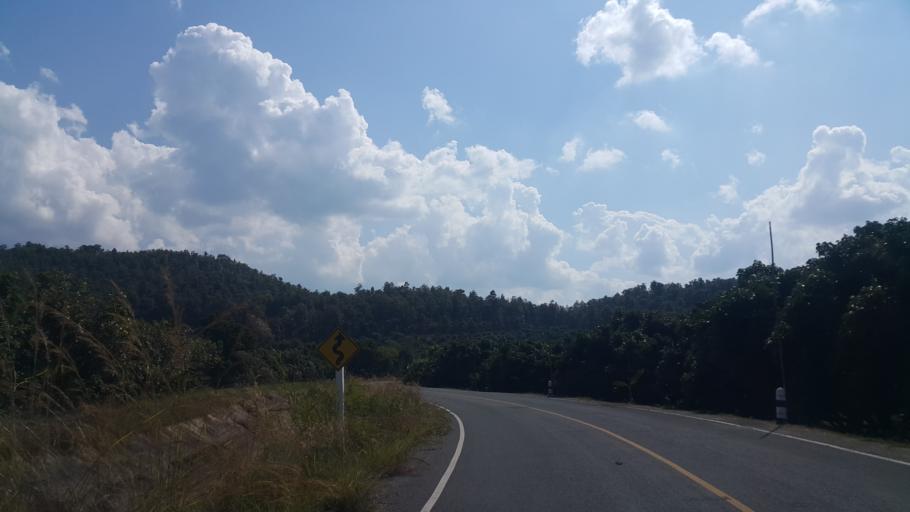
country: TH
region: Lamphun
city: Ban Thi
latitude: 18.6408
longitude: 99.1620
